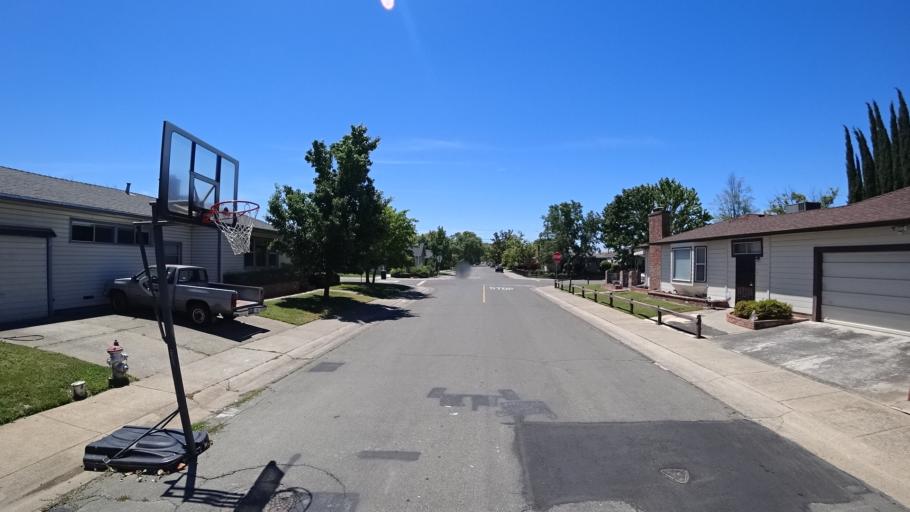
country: US
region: California
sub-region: Sacramento County
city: Sacramento
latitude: 38.5740
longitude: -121.4358
